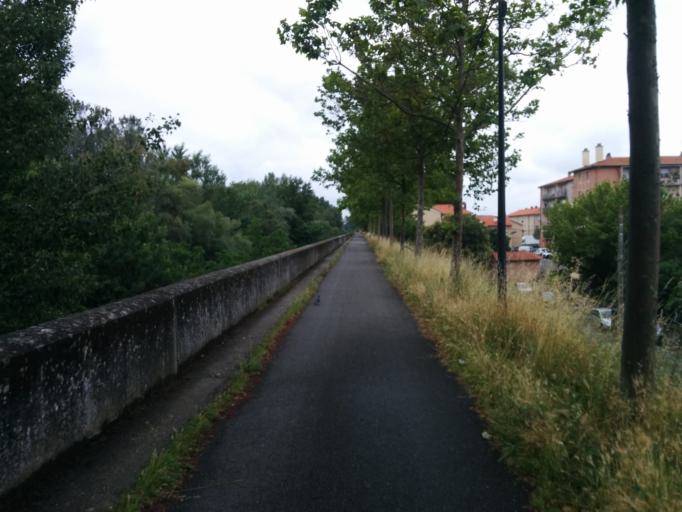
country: FR
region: Midi-Pyrenees
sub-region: Departement de la Haute-Garonne
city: Blagnac
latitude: 43.6113
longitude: 1.4100
